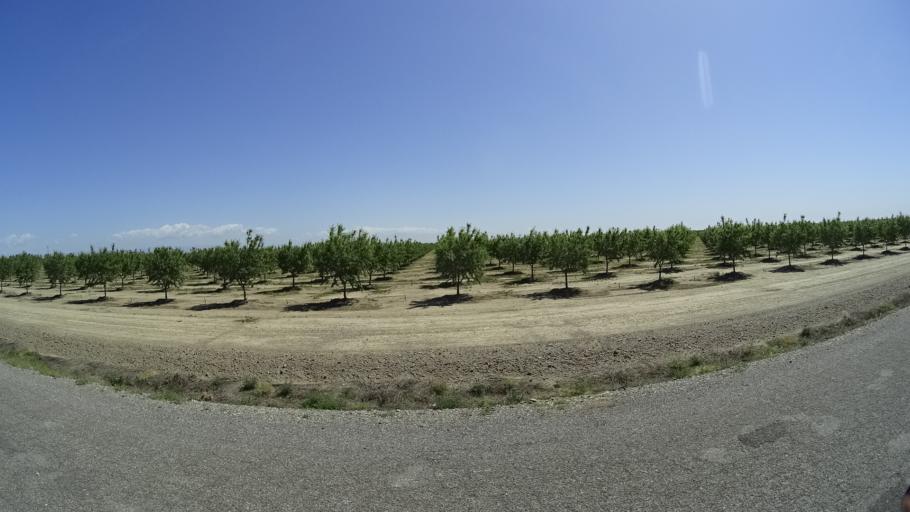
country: US
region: California
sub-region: Glenn County
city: Orland
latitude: 39.6875
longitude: -122.1220
